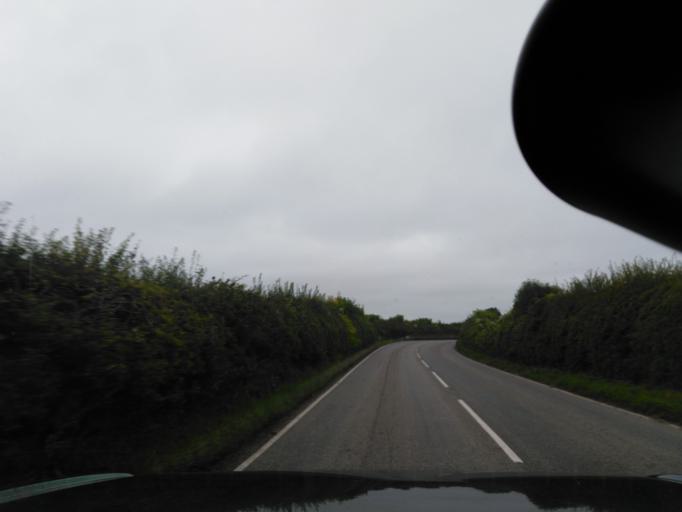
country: GB
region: England
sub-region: Dorset
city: Blandford Forum
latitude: 50.9132
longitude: -2.1954
